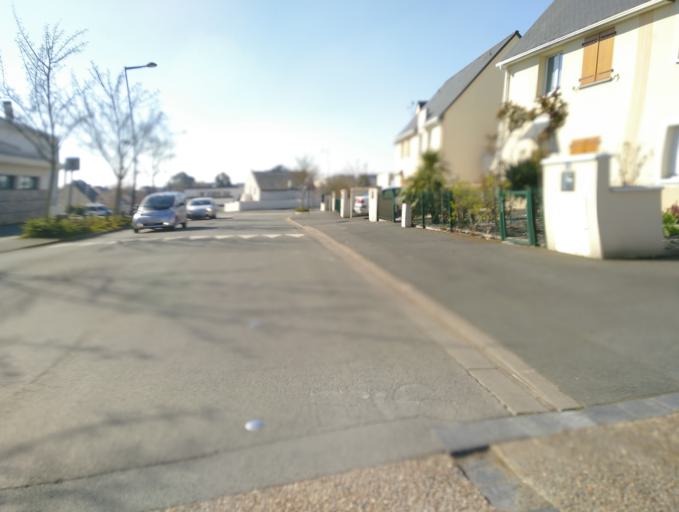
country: FR
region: Pays de la Loire
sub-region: Departement de Maine-et-Loire
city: Les Ponts-de-Ce
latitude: 47.4518
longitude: -0.5079
